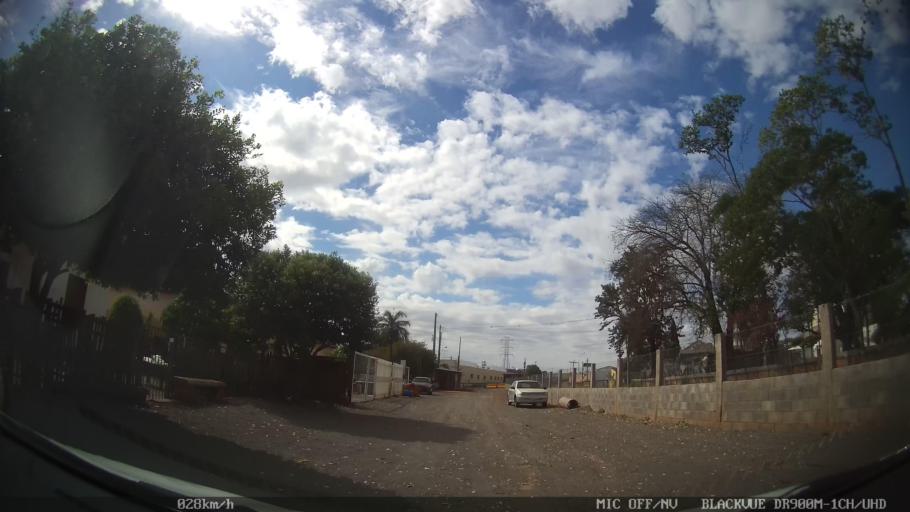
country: BR
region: Sao Paulo
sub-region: Bady Bassitt
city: Bady Bassitt
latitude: -20.8125
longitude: -49.5130
